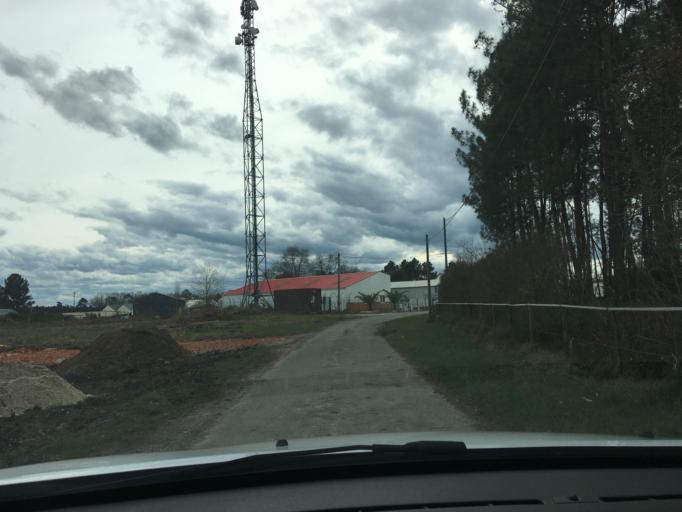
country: FR
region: Aquitaine
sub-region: Departement de la Gironde
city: Saint-Sauveur
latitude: 45.2219
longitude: -0.8714
